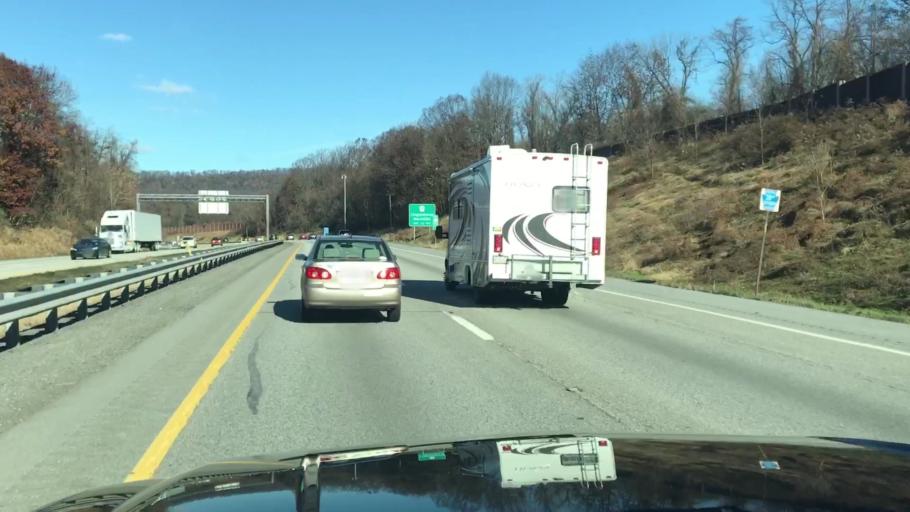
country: US
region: Pennsylvania
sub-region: Dauphin County
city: Harrisburg
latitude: 40.3175
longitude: -76.8826
